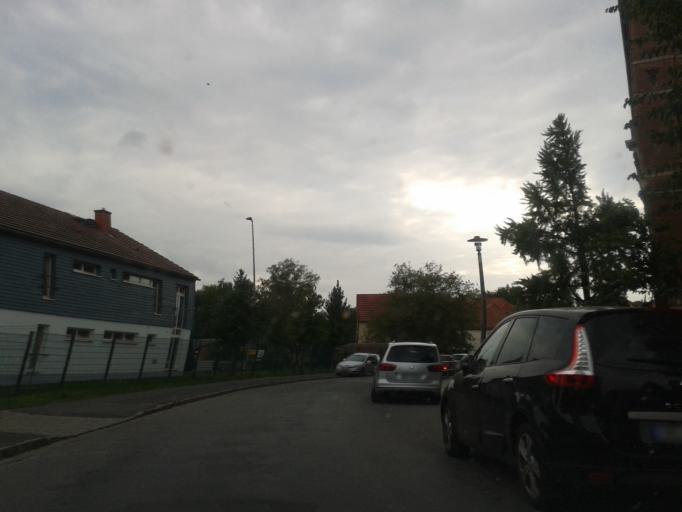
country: DE
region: Saxony
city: Dresden
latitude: 51.0546
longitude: 13.6859
